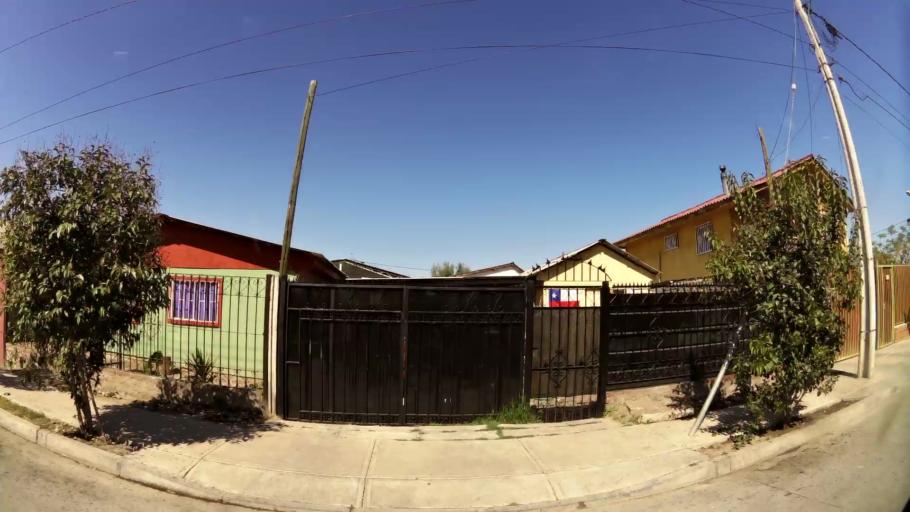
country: CL
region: Santiago Metropolitan
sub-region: Provincia de Maipo
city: San Bernardo
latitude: -33.6087
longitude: -70.7119
